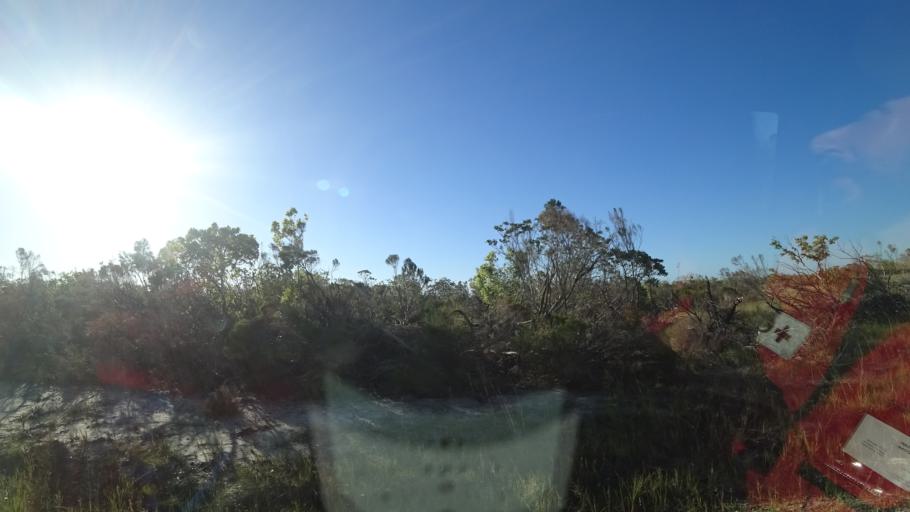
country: MZ
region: Sofala
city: Beira
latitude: -19.5767
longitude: 35.1938
